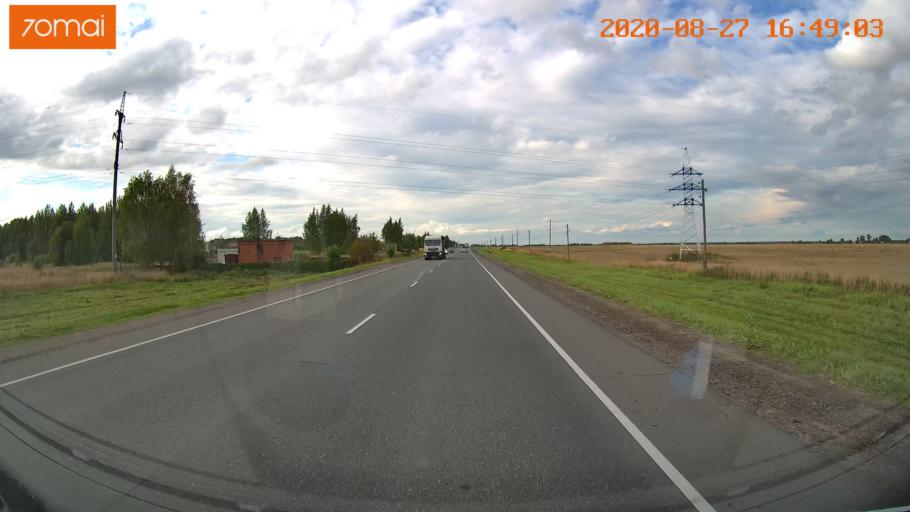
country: RU
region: Vladimir
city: Suzdal'
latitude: 56.4352
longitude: 40.4695
